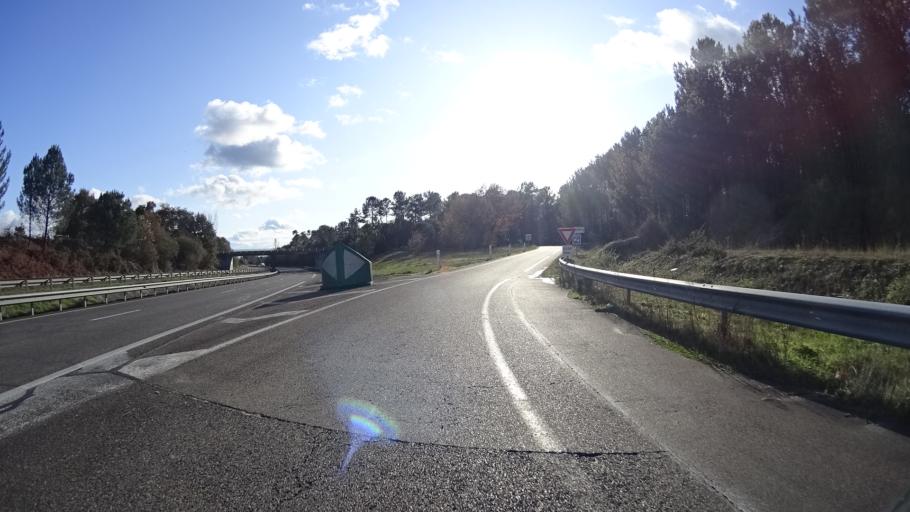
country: FR
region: Aquitaine
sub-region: Departement des Landes
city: Mees
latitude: 43.7338
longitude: -1.1023
